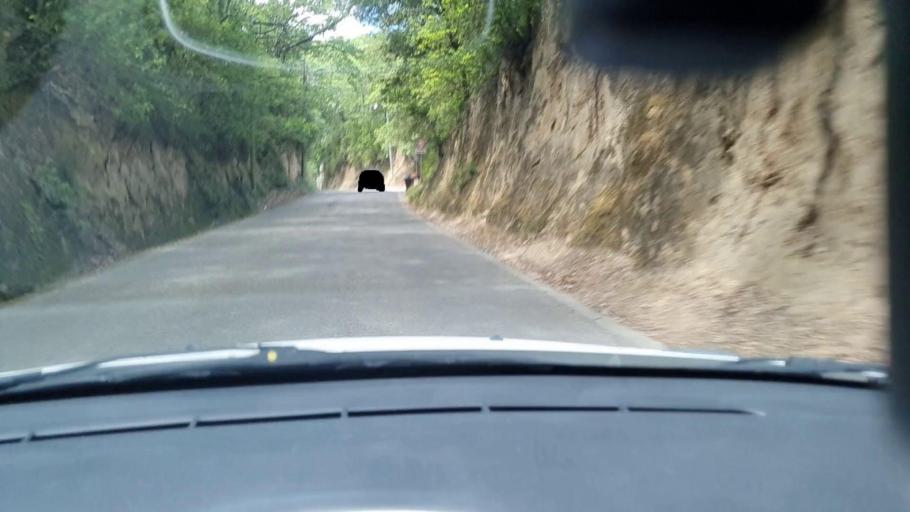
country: FR
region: Languedoc-Roussillon
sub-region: Departement du Gard
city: Cabrieres
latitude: 43.9544
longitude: 4.4724
